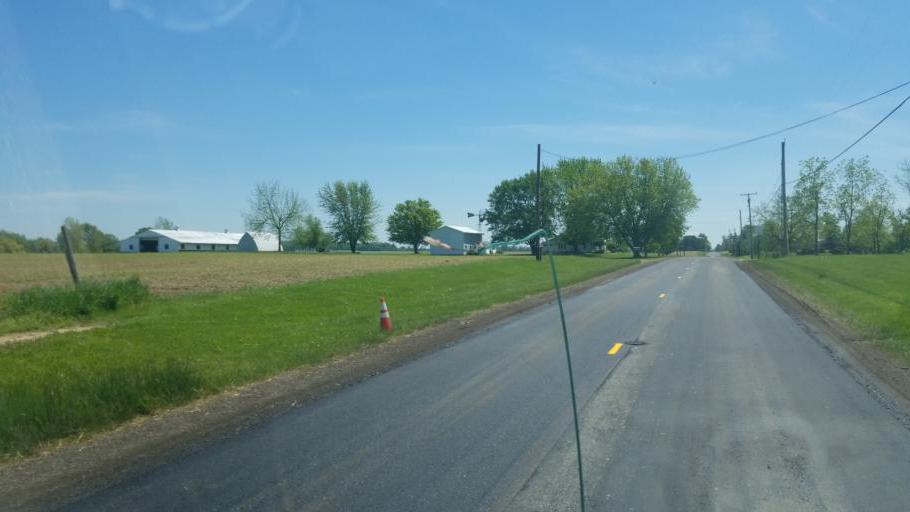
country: US
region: Ohio
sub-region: Huron County
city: Norwalk
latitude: 41.1973
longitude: -82.5902
